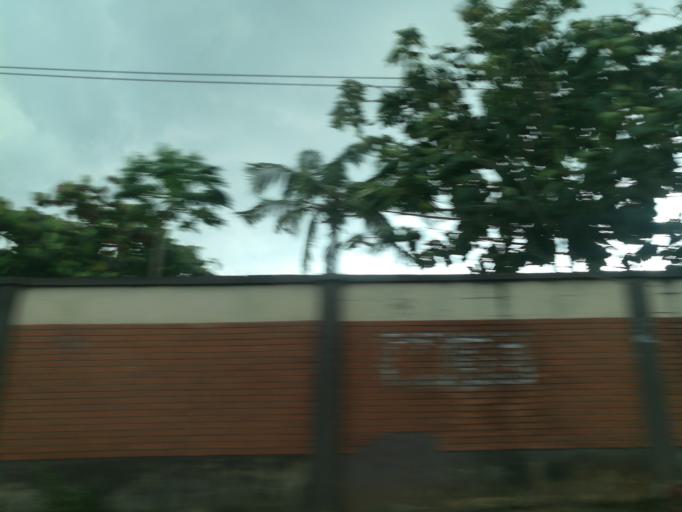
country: NG
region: Lagos
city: Ojota
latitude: 6.5996
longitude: 3.3801
